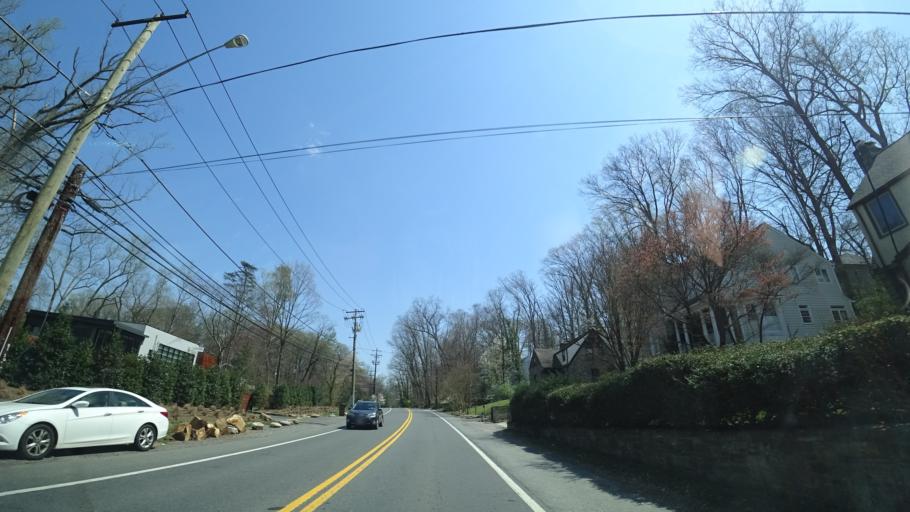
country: US
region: Maryland
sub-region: Montgomery County
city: Bethesda
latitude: 38.9962
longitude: -77.1285
